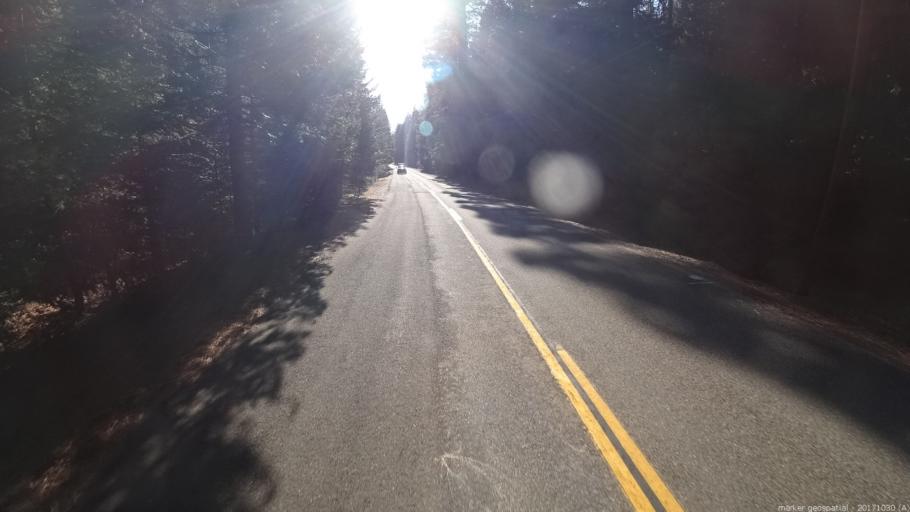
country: US
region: California
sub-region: Shasta County
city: Shingletown
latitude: 40.5338
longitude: -121.7414
